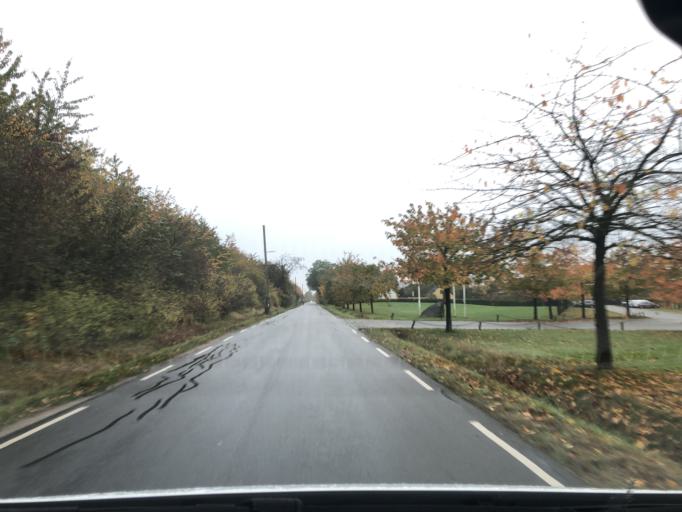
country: DK
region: Capital Region
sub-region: Tarnby Kommune
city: Tarnby
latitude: 55.5714
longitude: 12.5969
